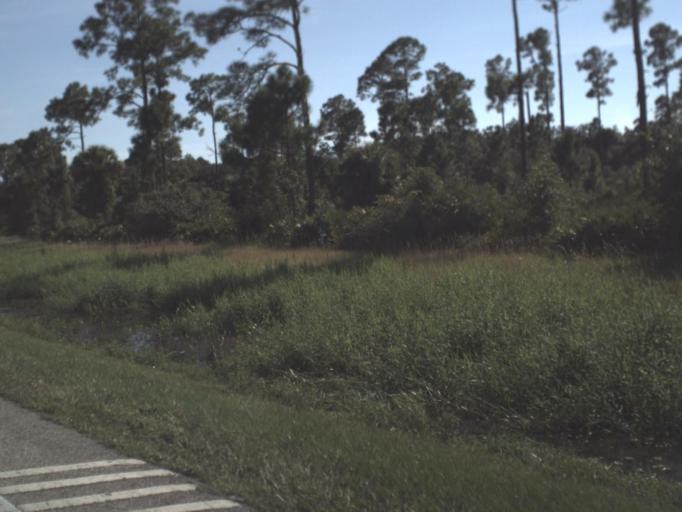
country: US
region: Florida
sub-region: Glades County
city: Moore Haven
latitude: 26.8988
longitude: -81.2390
